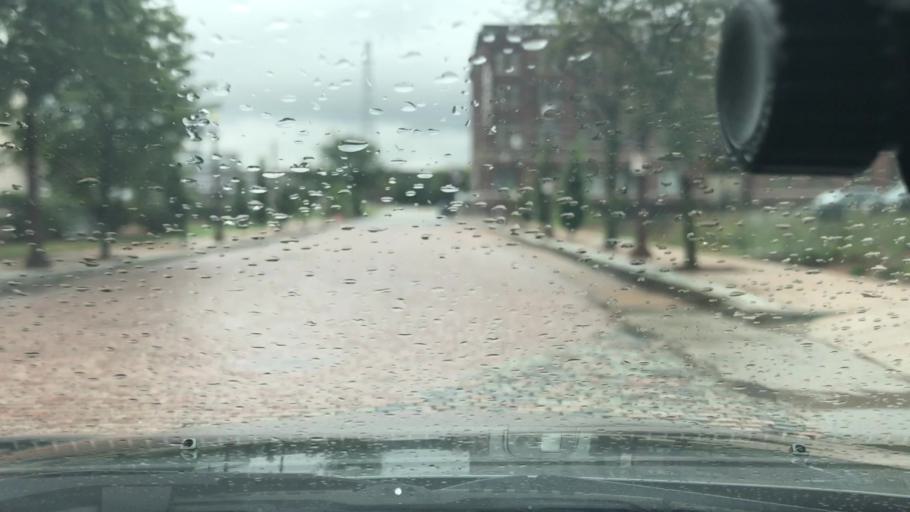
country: US
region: Missouri
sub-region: City of Saint Louis
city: St. Louis
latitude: 38.6289
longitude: -90.2095
